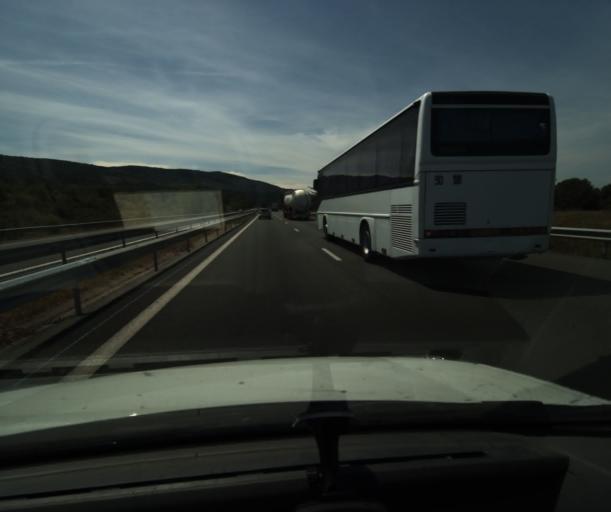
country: FR
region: Languedoc-Roussillon
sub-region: Departement de l'Aude
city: Capendu
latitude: 43.1794
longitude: 2.5523
